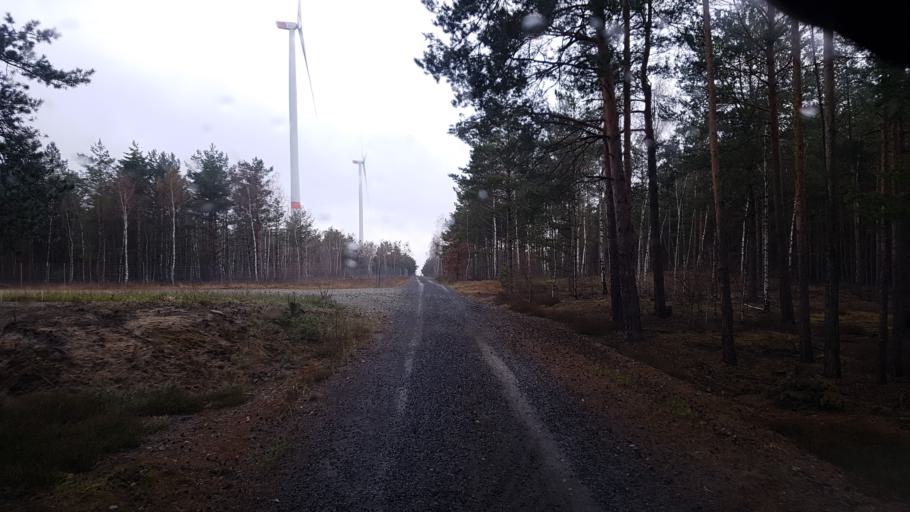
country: DE
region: Brandenburg
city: Grossraschen
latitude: 51.6189
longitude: 13.9674
